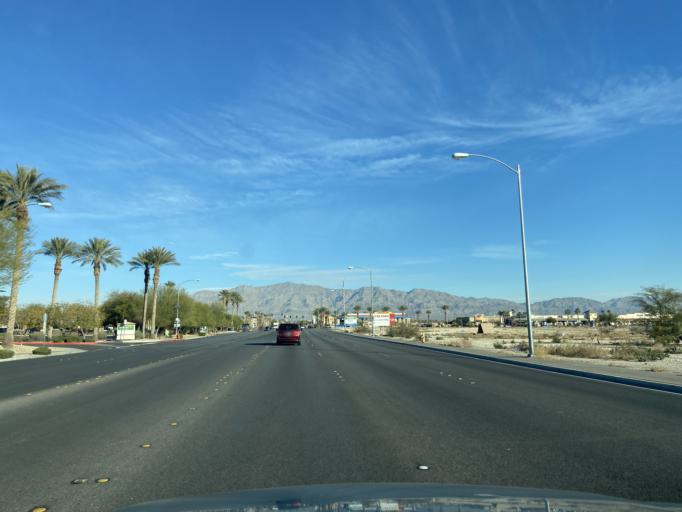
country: US
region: Nevada
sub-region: Clark County
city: North Las Vegas
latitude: 36.2592
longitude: -115.1799
